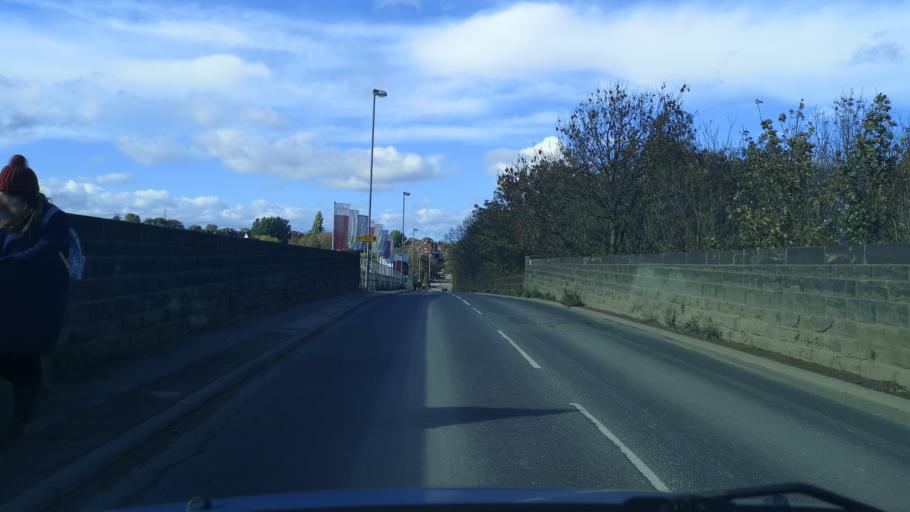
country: GB
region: England
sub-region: City and Borough of Wakefield
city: Normanton
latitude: 53.7021
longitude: -1.4225
